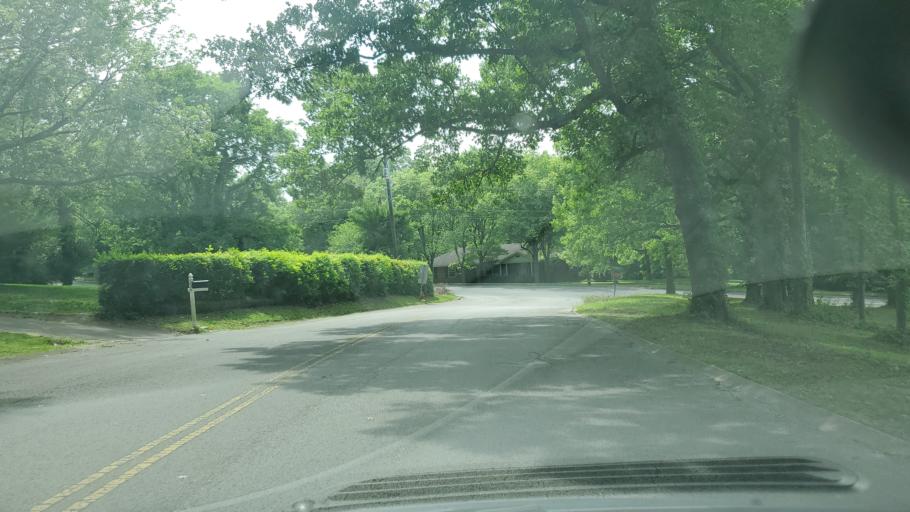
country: US
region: Tennessee
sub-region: Davidson County
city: Oak Hill
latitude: 36.1133
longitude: -86.6989
